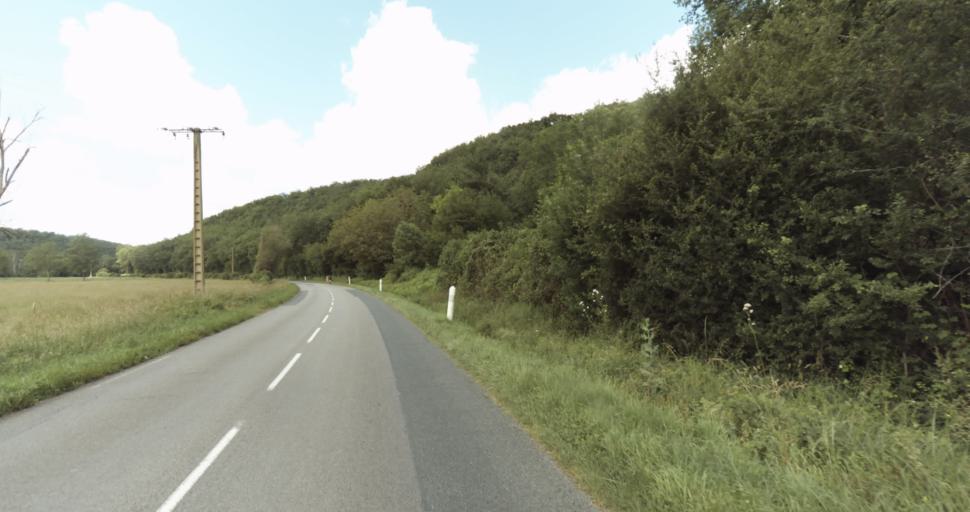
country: FR
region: Aquitaine
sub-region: Departement de la Dordogne
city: Beaumont-du-Perigord
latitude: 44.7986
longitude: 0.7484
